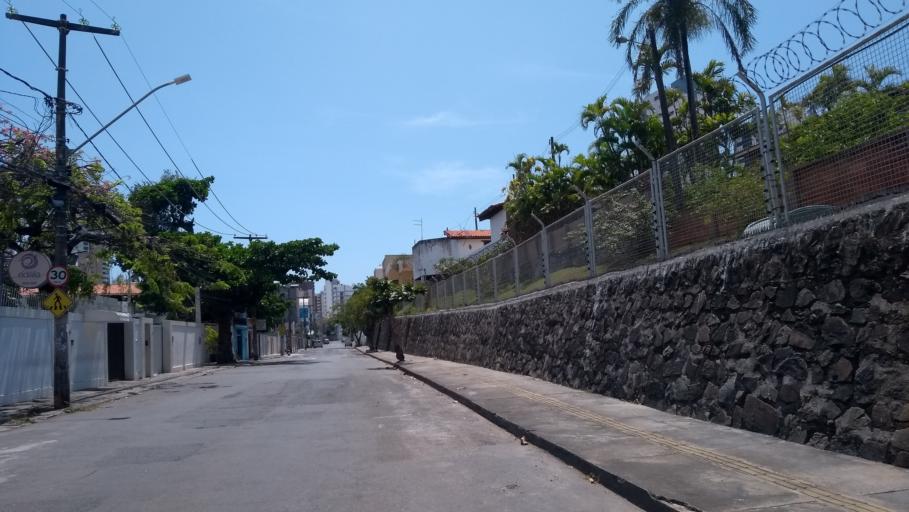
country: BR
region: Bahia
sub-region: Salvador
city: Salvador
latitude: -12.9906
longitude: -38.4587
